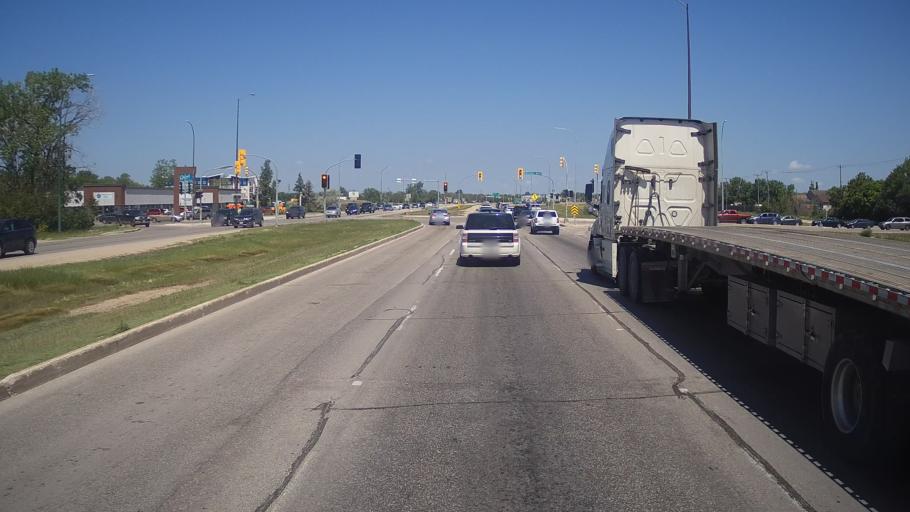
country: CA
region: Manitoba
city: Winnipeg
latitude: 49.9216
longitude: -97.0483
